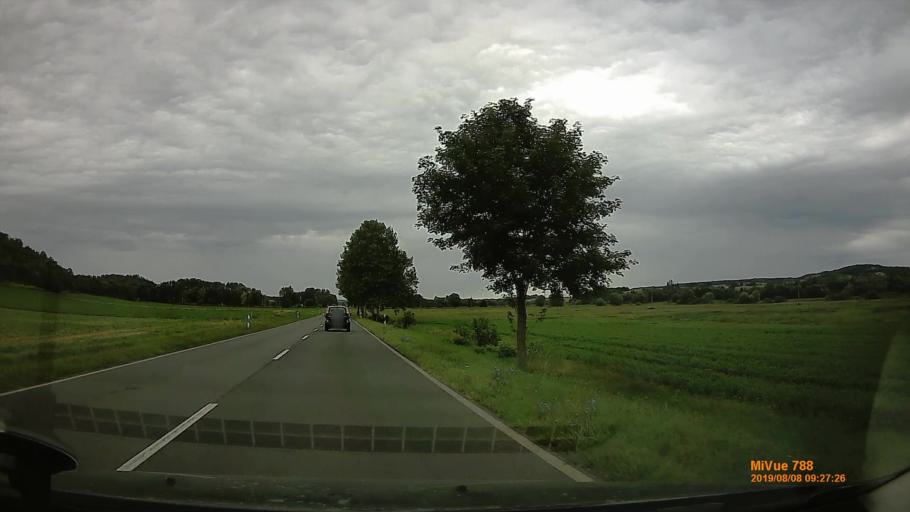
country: HU
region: Zala
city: Zalaegerszeg
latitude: 46.9479
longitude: 16.8488
